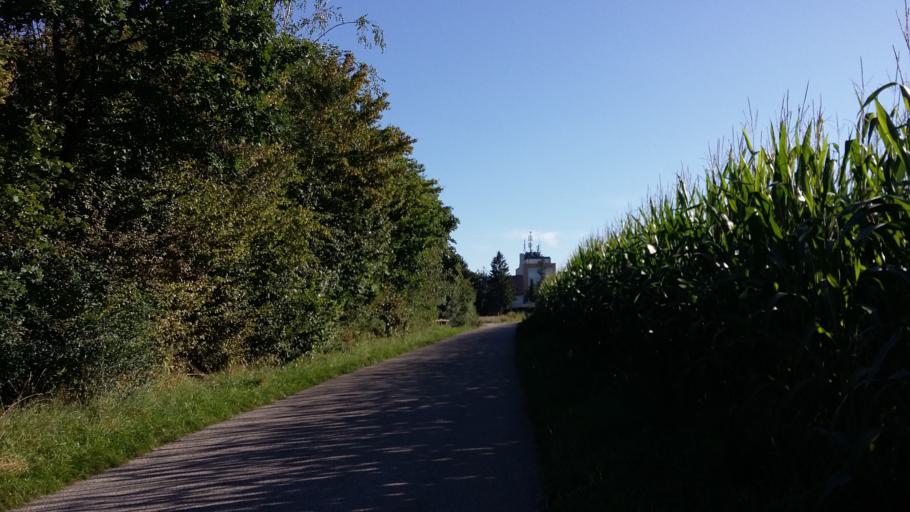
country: DE
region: Bavaria
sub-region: Upper Bavaria
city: Gauting
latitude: 48.0757
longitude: 11.3891
